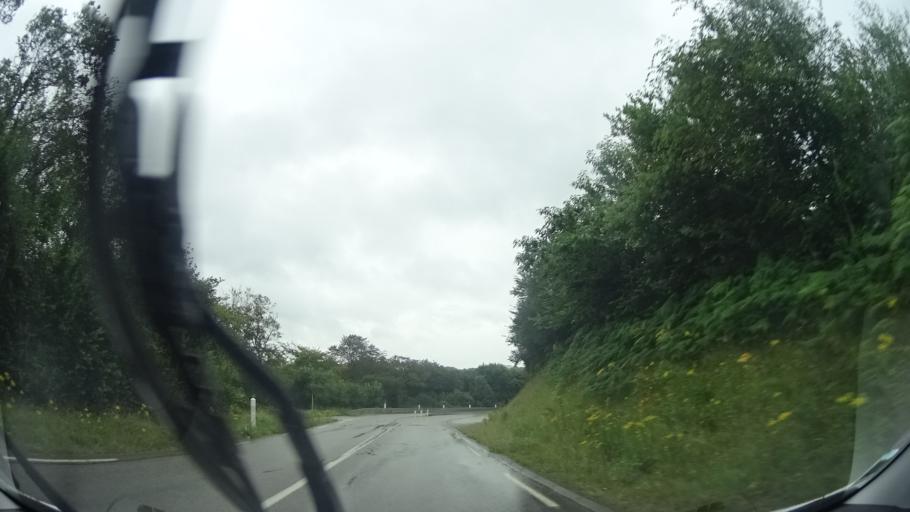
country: FR
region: Lower Normandy
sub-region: Departement de la Manche
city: Beaumont-Hague
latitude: 49.6146
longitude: -1.7894
